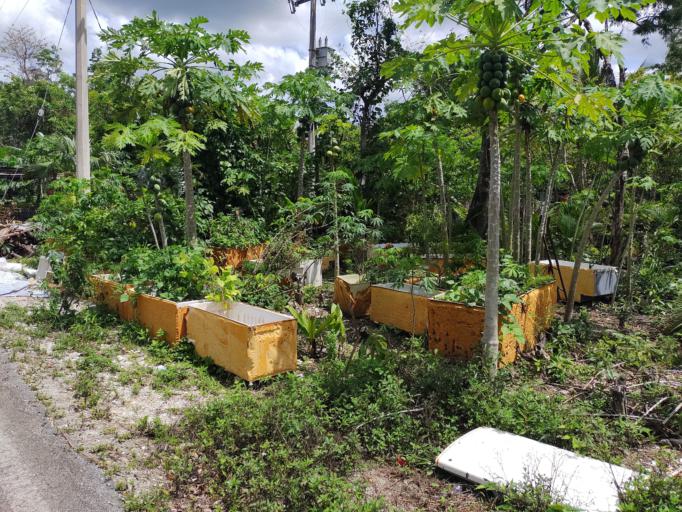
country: MX
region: Quintana Roo
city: San Miguel de Cozumel
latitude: 20.4696
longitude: -86.8989
